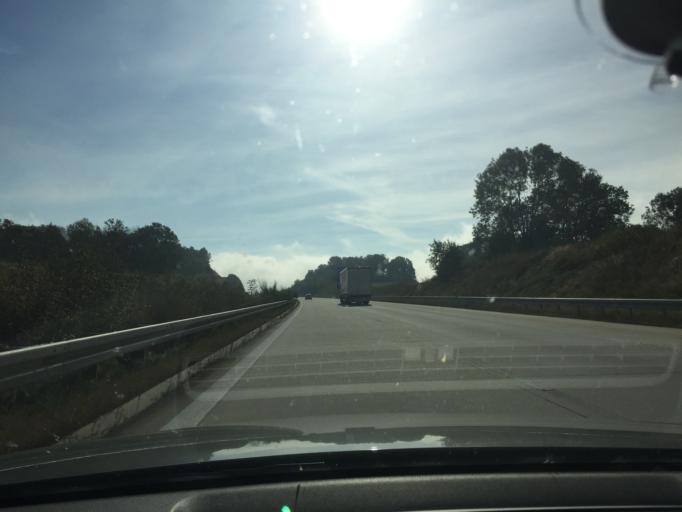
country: DE
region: Saxony
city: Liebstadt
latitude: 50.8402
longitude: 13.8822
